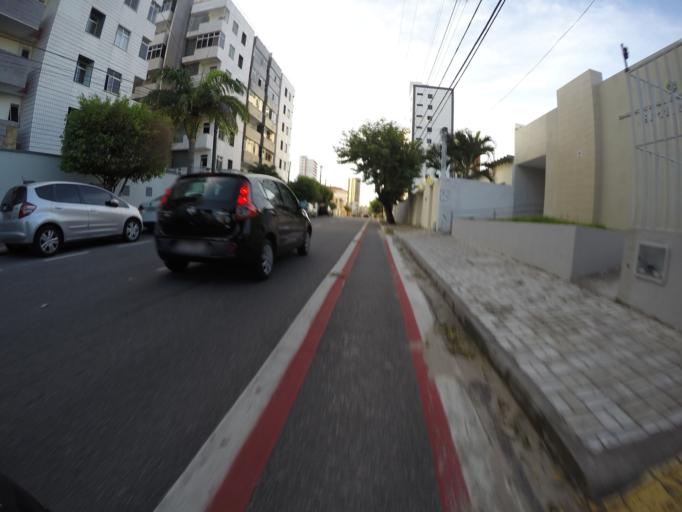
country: BR
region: Ceara
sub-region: Fortaleza
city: Fortaleza
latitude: -3.7440
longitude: -38.5143
